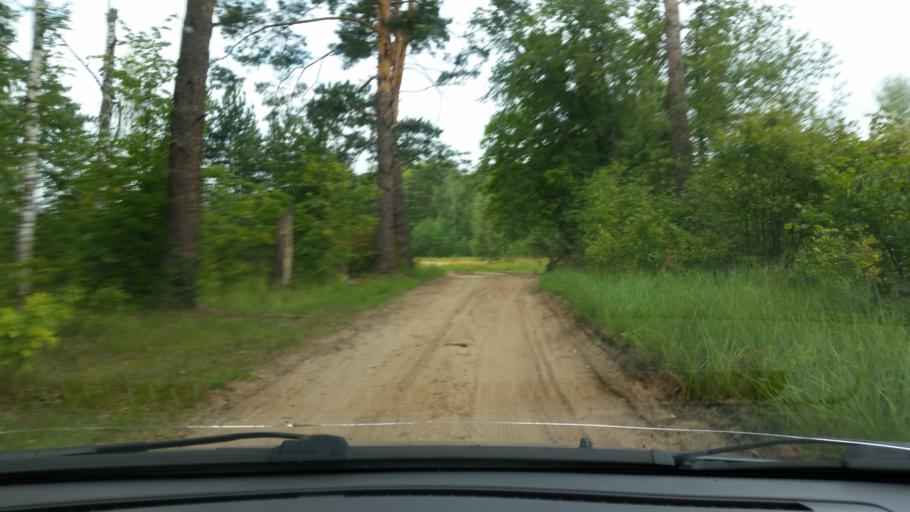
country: RU
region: Moskovskaya
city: Bol'shoye Gryzlovo
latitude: 54.8548
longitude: 37.7141
